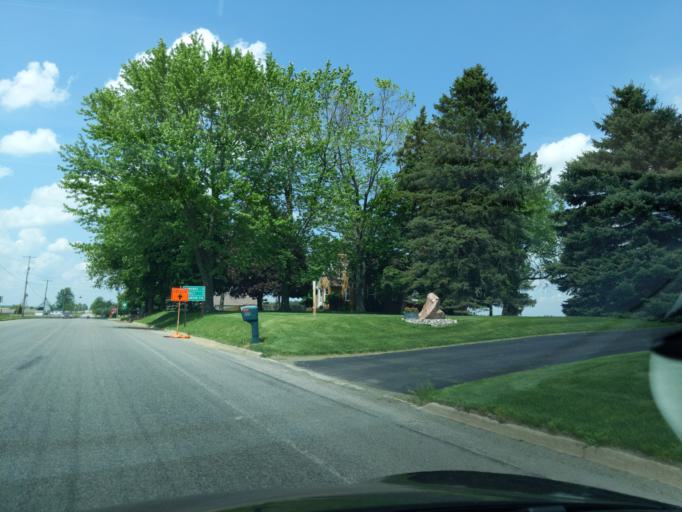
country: US
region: Michigan
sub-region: Ingham County
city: Mason
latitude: 42.6388
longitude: -84.4330
